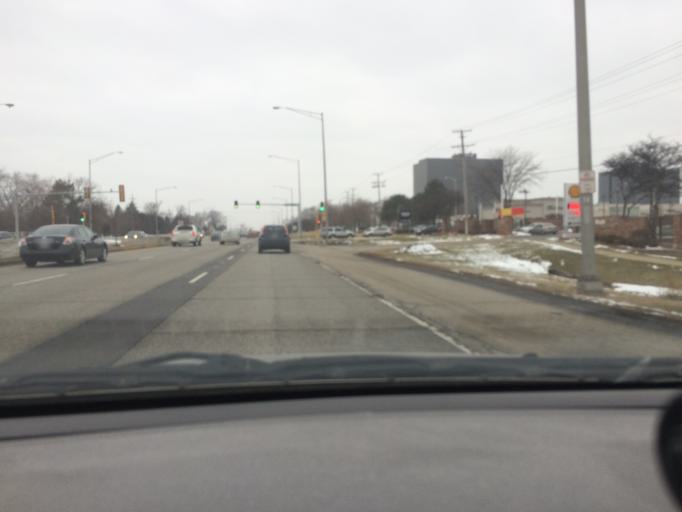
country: US
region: Illinois
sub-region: Cook County
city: Hoffman Estates
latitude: 42.0382
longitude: -88.0378
